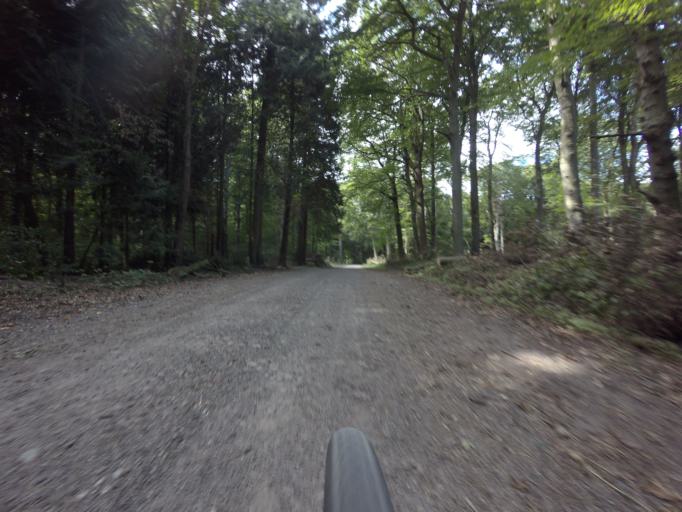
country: DK
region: Zealand
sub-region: Vordingborg Kommune
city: Stege
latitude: 55.0205
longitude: 12.3902
